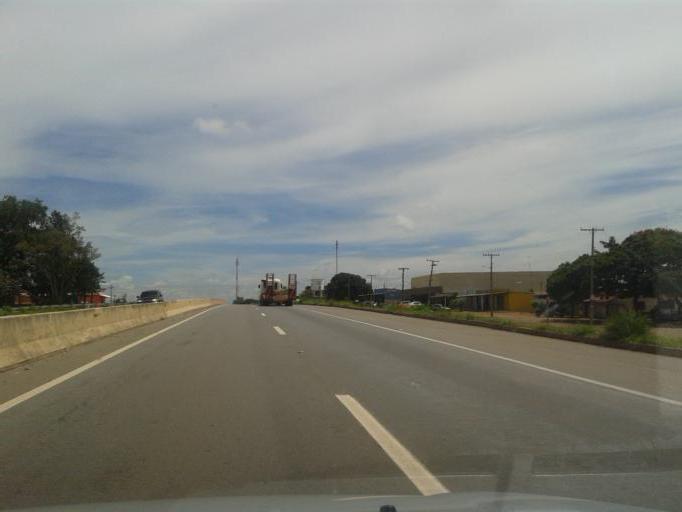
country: BR
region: Goias
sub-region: Hidrolandia
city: Hidrolandia
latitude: -16.9733
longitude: -49.2309
